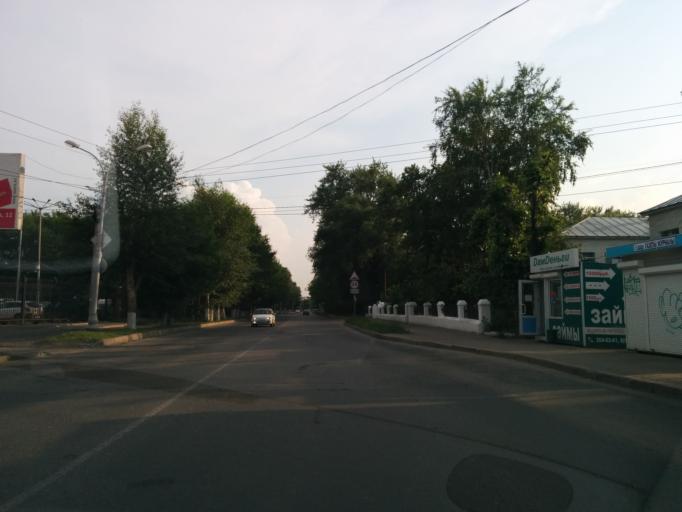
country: RU
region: Perm
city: Perm
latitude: 58.0252
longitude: 56.2947
